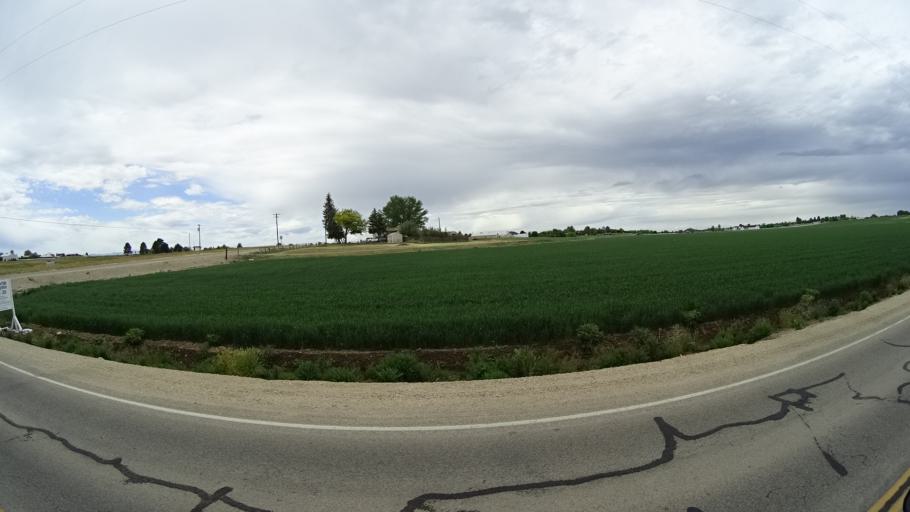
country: US
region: Idaho
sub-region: Ada County
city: Meridian
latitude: 43.5618
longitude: -116.4139
